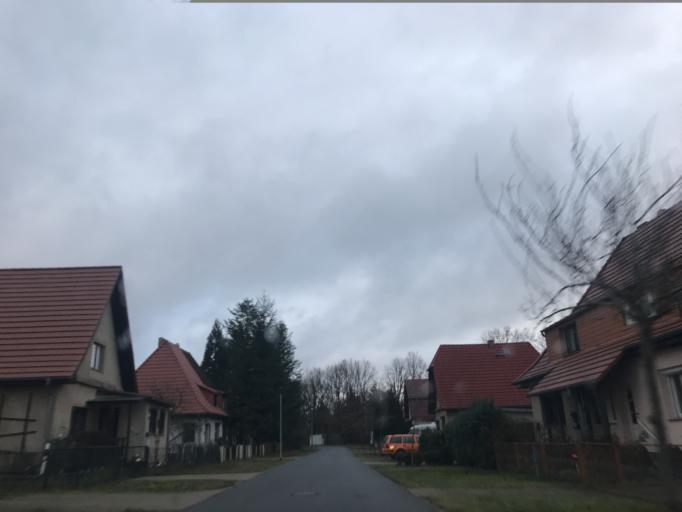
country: DE
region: Brandenburg
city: Rheinsberg
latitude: 53.0915
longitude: 12.8965
